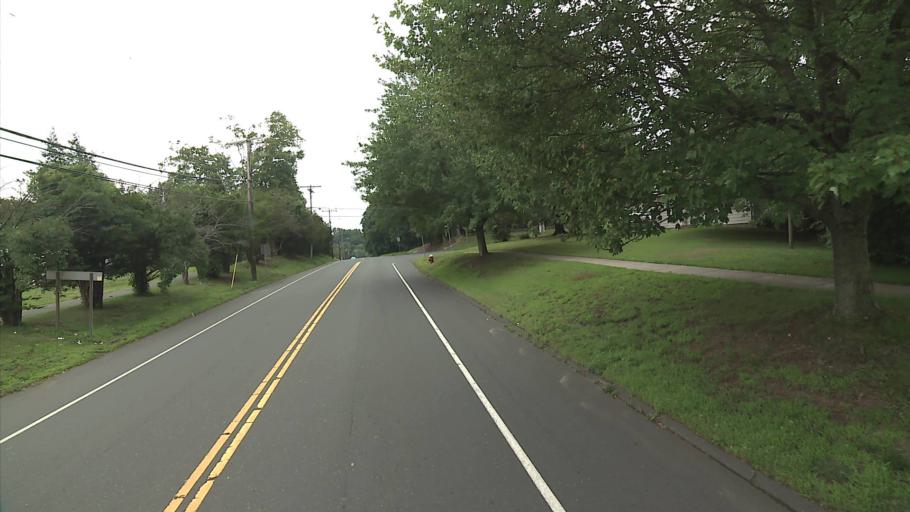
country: US
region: Connecticut
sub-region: Hartford County
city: Wethersfield
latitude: 41.6610
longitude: -72.6392
